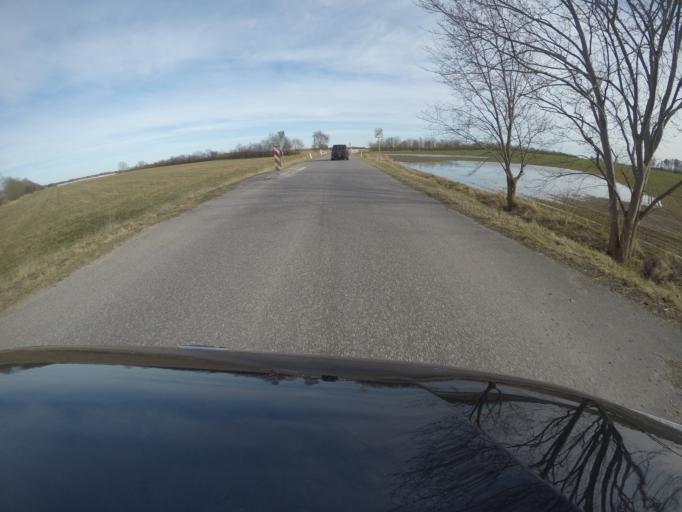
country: DK
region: Capital Region
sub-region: Halsnaes Kommune
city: Liseleje
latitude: 55.9838
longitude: 11.9457
